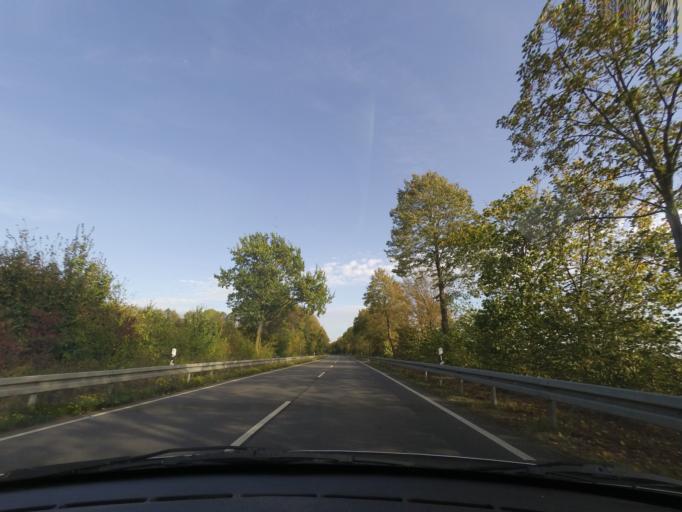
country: DE
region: North Rhine-Westphalia
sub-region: Regierungsbezirk Dusseldorf
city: Neubrueck
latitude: 51.1686
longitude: 6.6251
